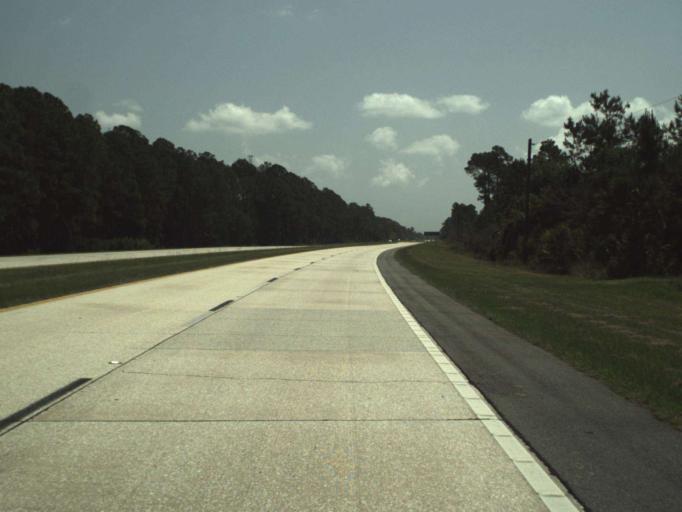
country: US
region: Florida
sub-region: Volusia County
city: Samsula-Spruce Creek
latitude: 29.1321
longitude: -81.1535
